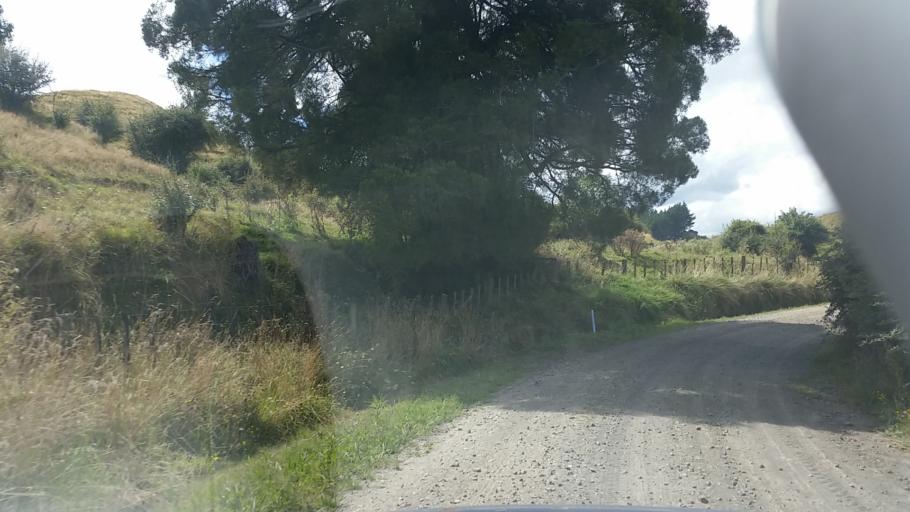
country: NZ
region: Taranaki
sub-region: South Taranaki District
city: Eltham
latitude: -39.2567
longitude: 174.5677
